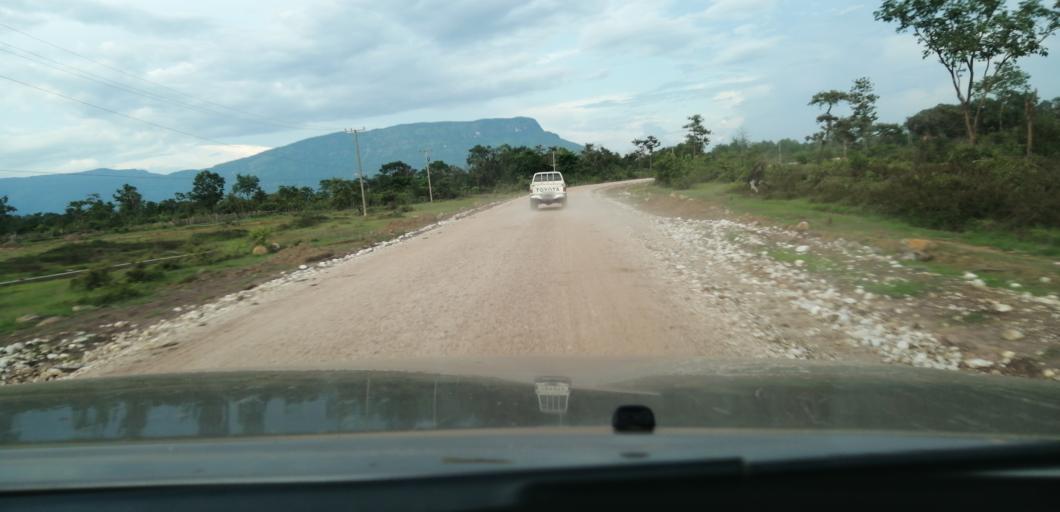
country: LA
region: Attapu
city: Attapu
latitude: 14.7101
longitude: 106.4882
